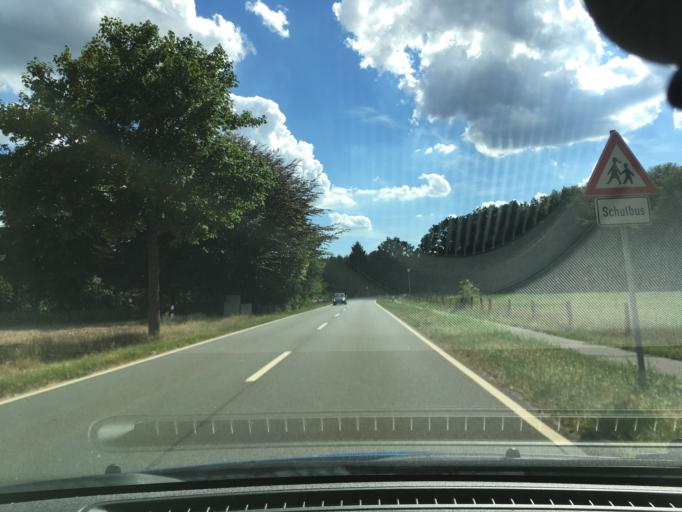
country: DE
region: Lower Saxony
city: Wriedel
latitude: 52.9893
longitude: 10.2550
